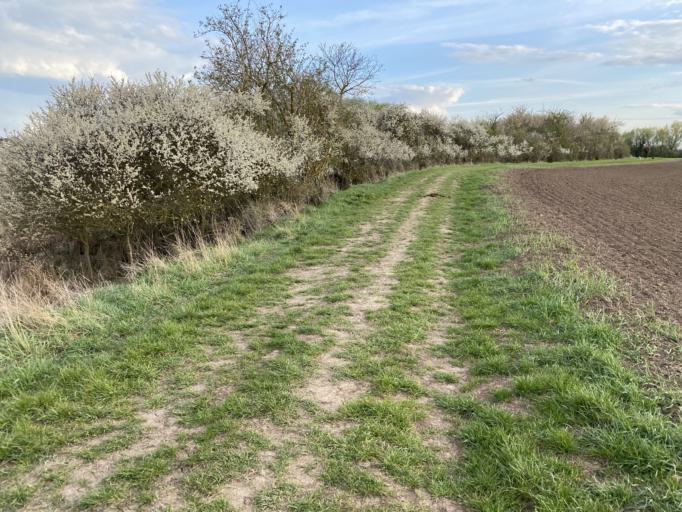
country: DE
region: Hesse
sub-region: Regierungsbezirk Darmstadt
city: Gross-Gerau
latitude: 49.9091
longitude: 8.4701
